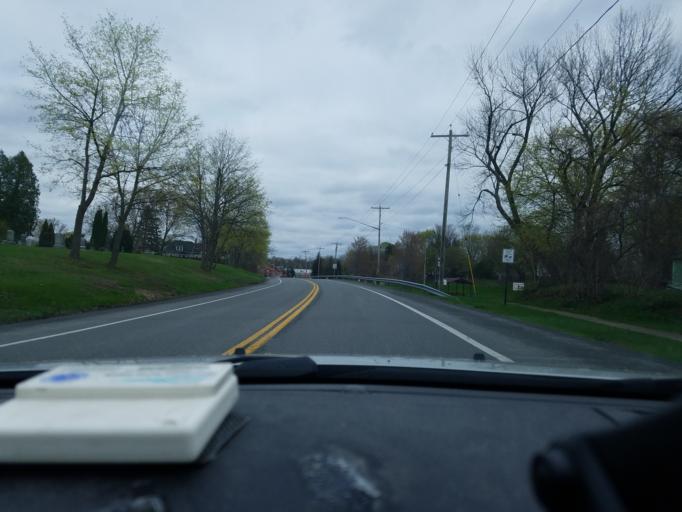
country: US
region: New York
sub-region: Onondaga County
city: North Syracuse
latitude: 43.1326
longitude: -76.1278
